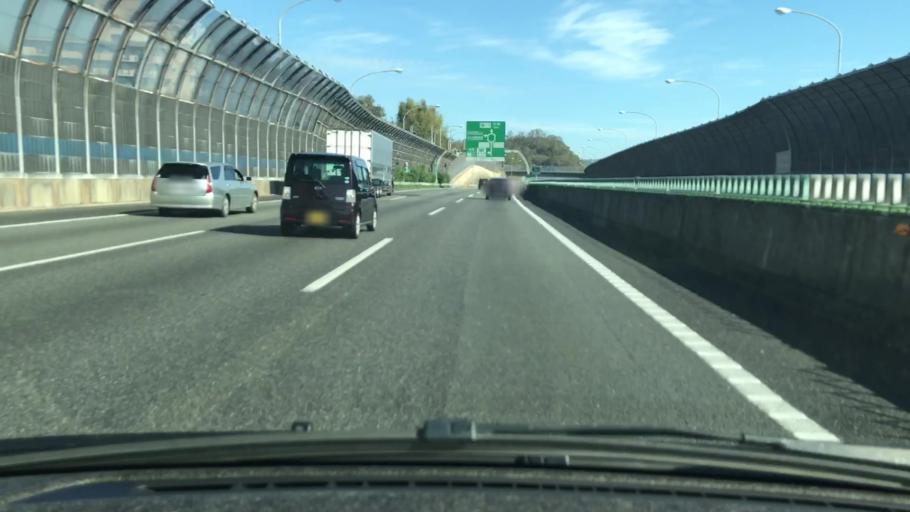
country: JP
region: Osaka
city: Takatsuki
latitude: 34.8508
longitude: 135.5822
